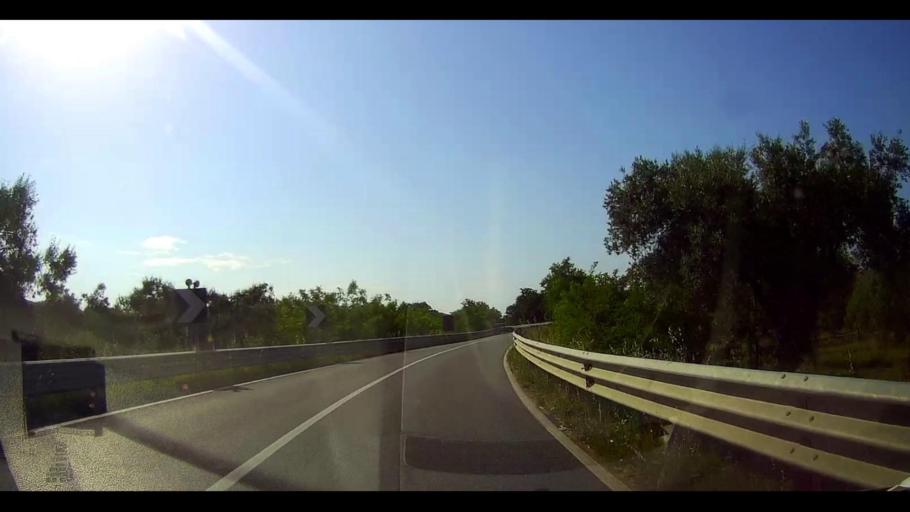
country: IT
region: Calabria
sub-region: Provincia di Cosenza
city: Cariati
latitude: 39.4823
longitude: 16.9777
